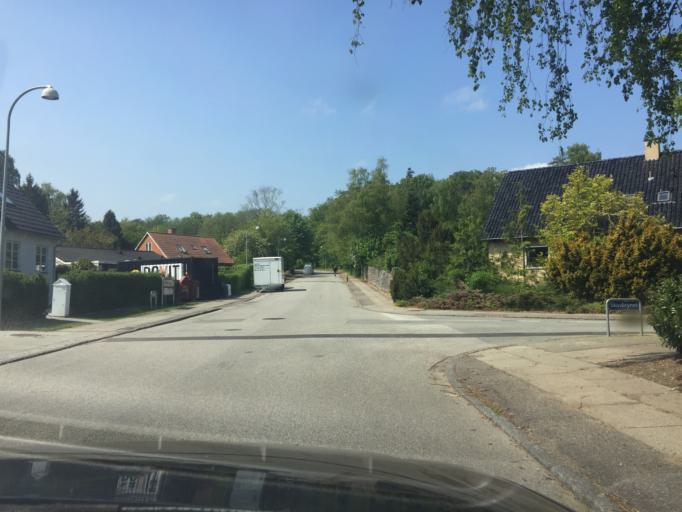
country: DK
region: Capital Region
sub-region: Herlev Kommune
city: Herlev
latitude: 55.7663
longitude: 12.4362
